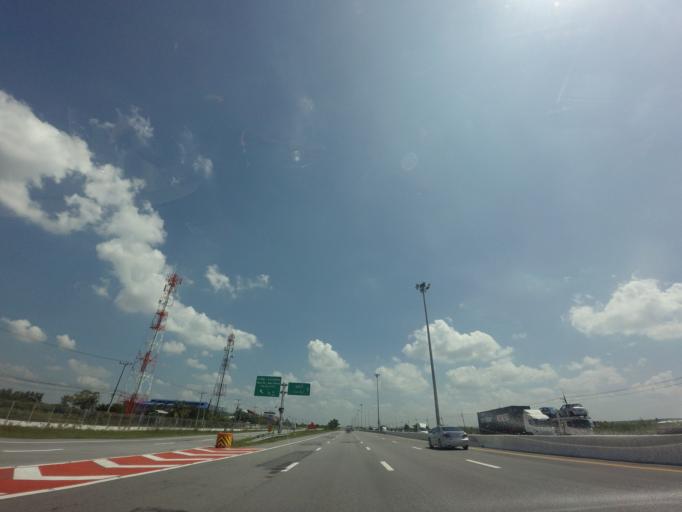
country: TH
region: Chachoengsao
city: Bang Pakong
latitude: 13.6054
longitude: 100.9446
